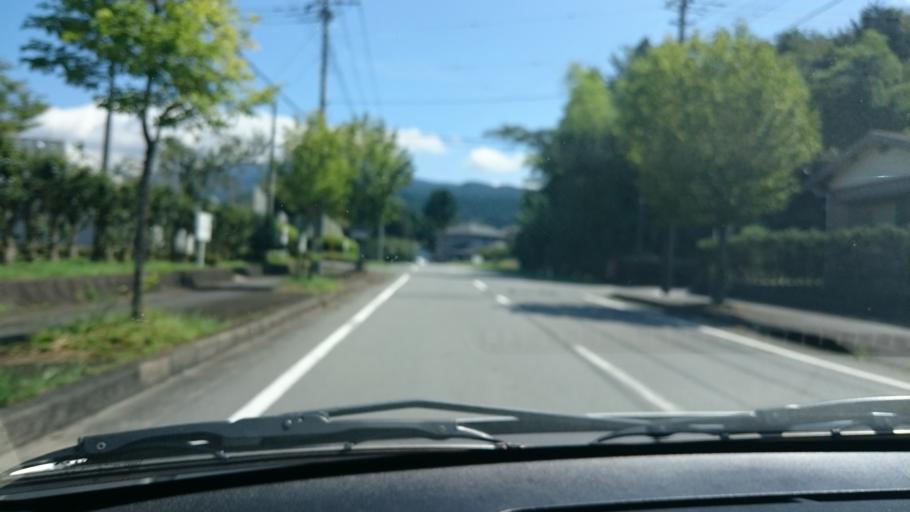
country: JP
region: Shizuoka
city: Gotemba
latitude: 35.2819
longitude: 138.9290
